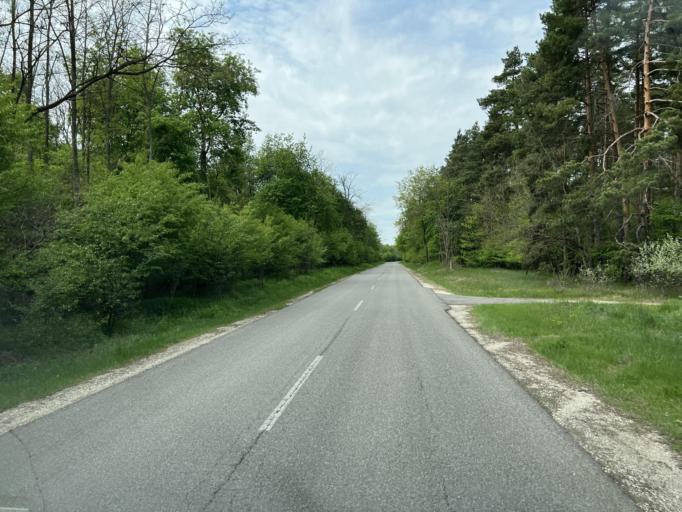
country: HU
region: Pest
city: Csemo
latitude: 47.1413
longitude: 19.6352
